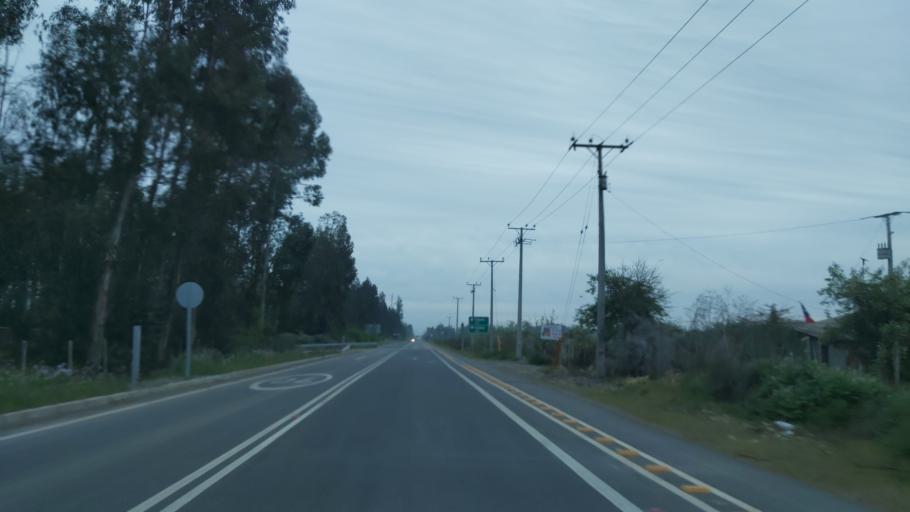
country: CL
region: Maule
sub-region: Provincia de Linares
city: Colbun
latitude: -35.6814
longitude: -71.4728
